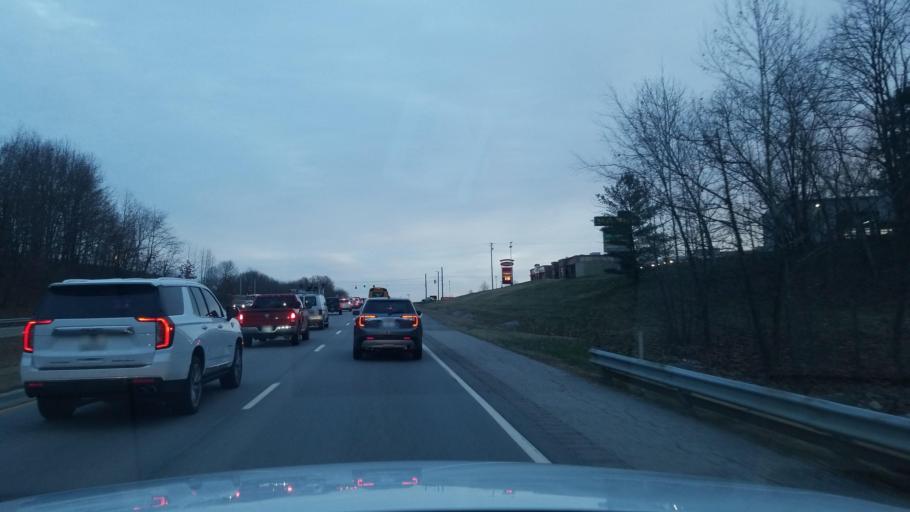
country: US
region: Indiana
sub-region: Vanderburgh County
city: Evansville
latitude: 37.9738
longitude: -87.6487
